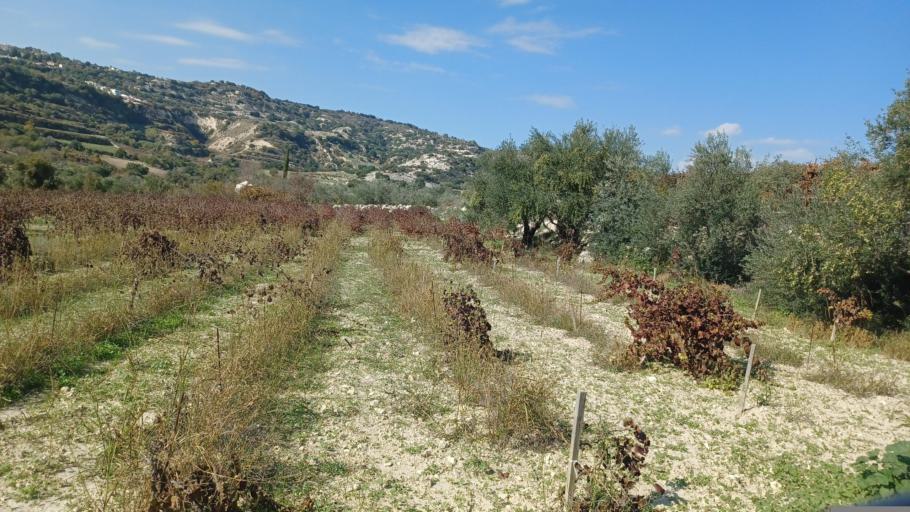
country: CY
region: Pafos
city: Mesogi
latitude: 34.8486
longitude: 32.5134
